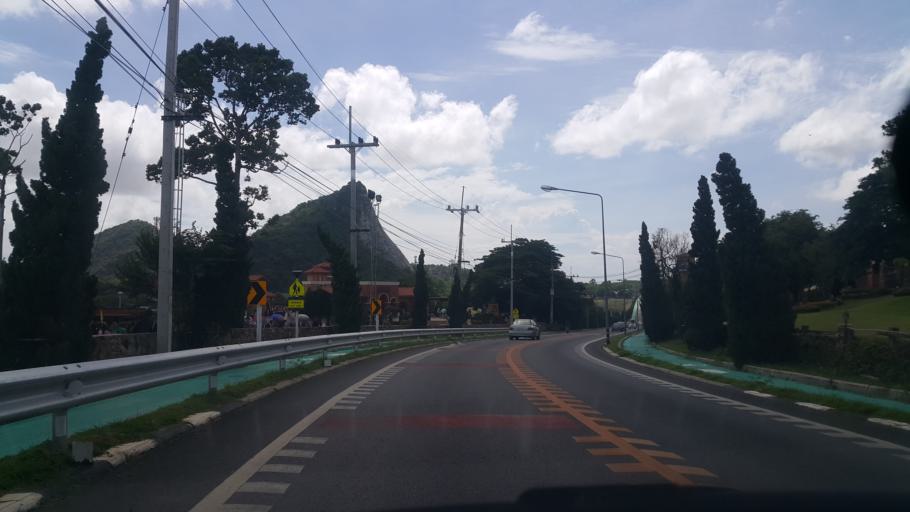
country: TH
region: Rayong
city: Ban Chang
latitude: 12.7600
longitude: 100.9652
